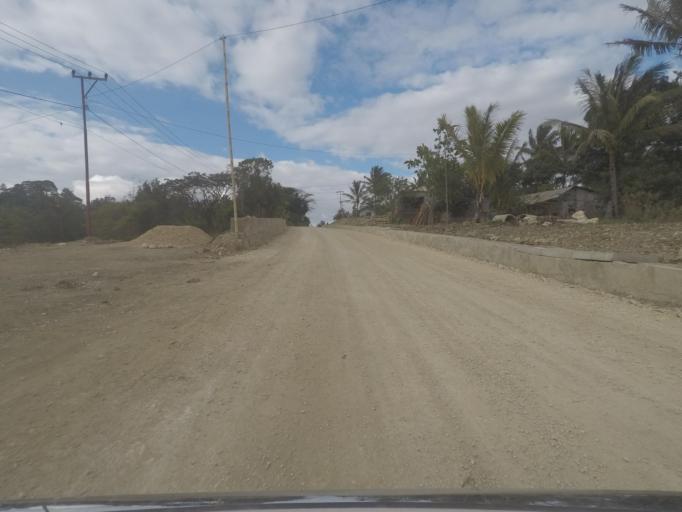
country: TL
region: Baucau
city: Venilale
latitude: -8.6396
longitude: 126.3769
